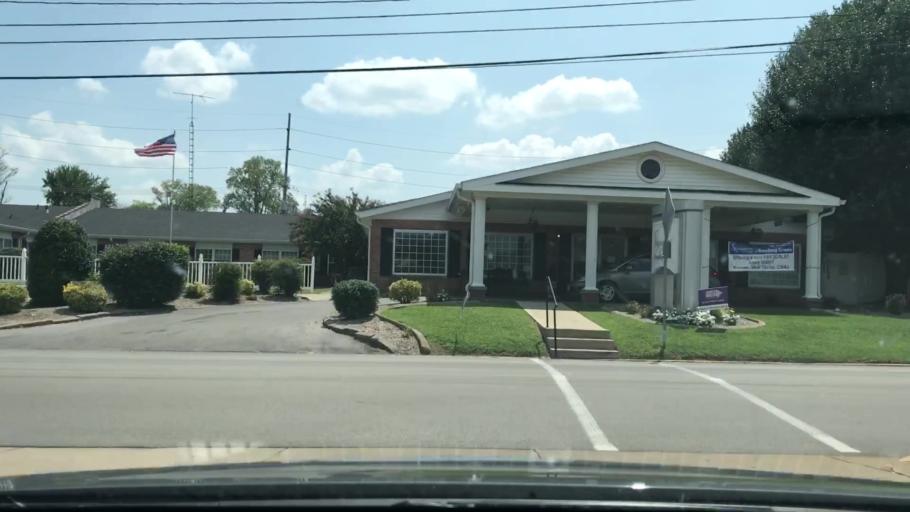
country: US
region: Kentucky
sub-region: Warren County
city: Bowling Green
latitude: 36.9929
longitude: -86.4333
